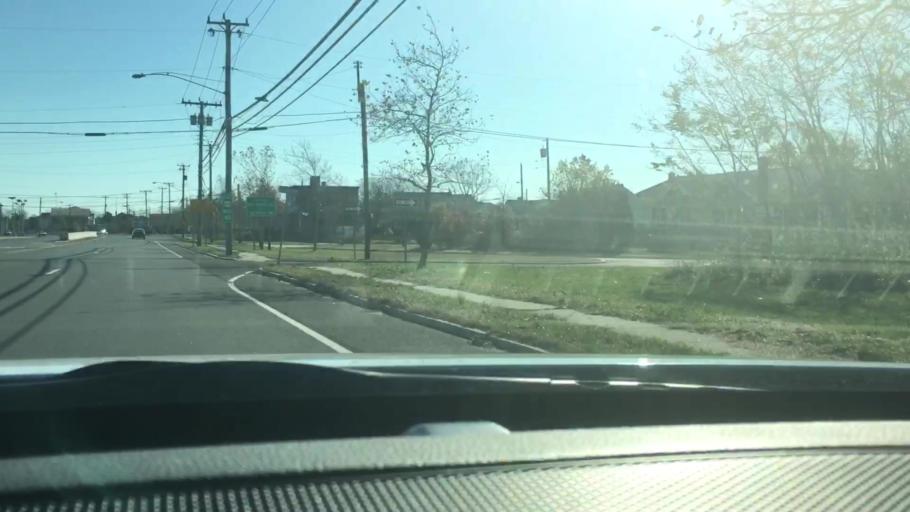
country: US
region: New Jersey
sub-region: Atlantic County
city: Pleasantville
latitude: 39.3870
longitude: -74.5163
